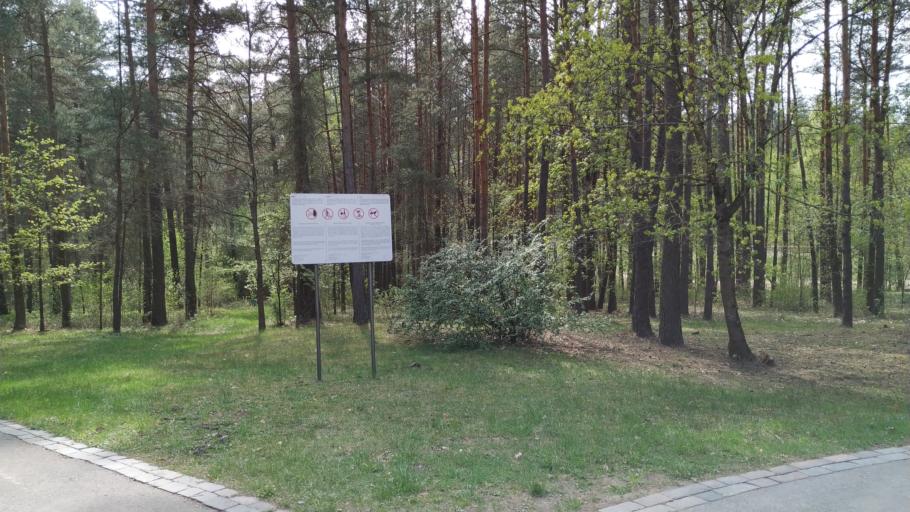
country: LT
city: Baltoji Voke
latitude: 54.6273
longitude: 25.1620
